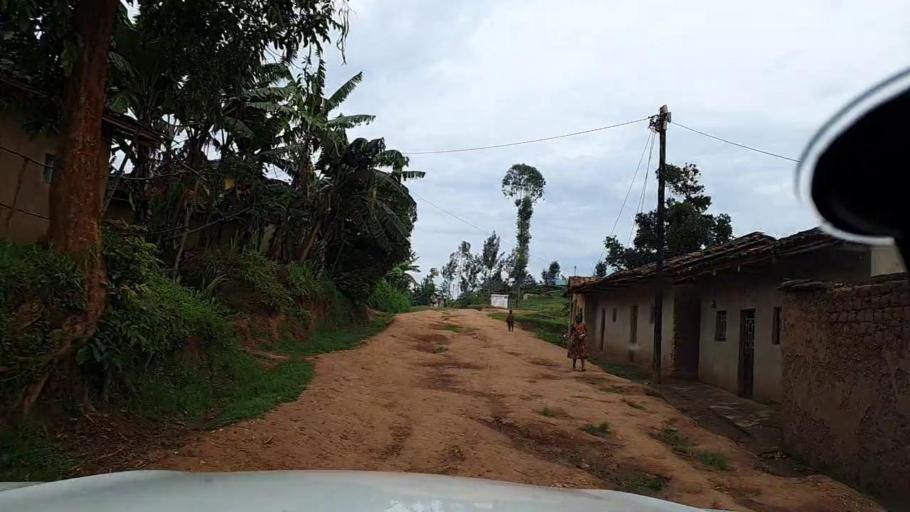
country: RW
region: Southern Province
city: Gitarama
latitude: -2.1159
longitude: 29.6395
